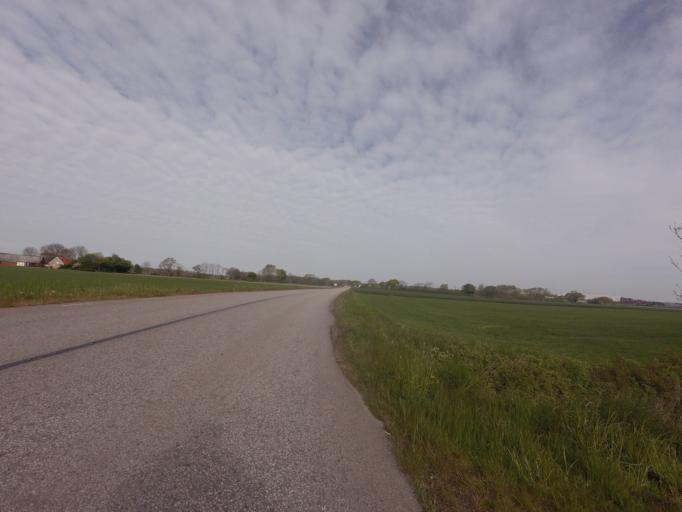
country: SE
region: Skane
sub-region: Hoganas Kommun
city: Hoganas
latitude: 56.1859
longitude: 12.5917
